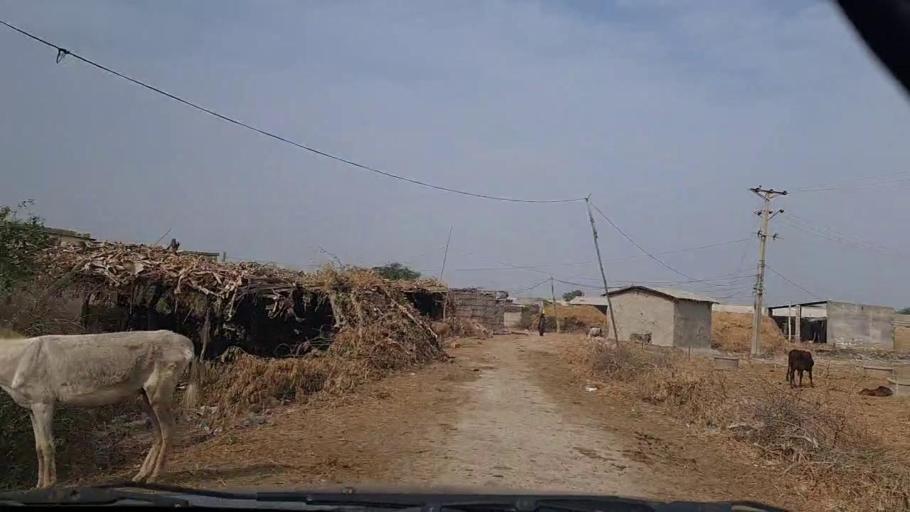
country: PK
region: Sindh
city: Thatta
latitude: 24.5873
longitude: 67.9069
